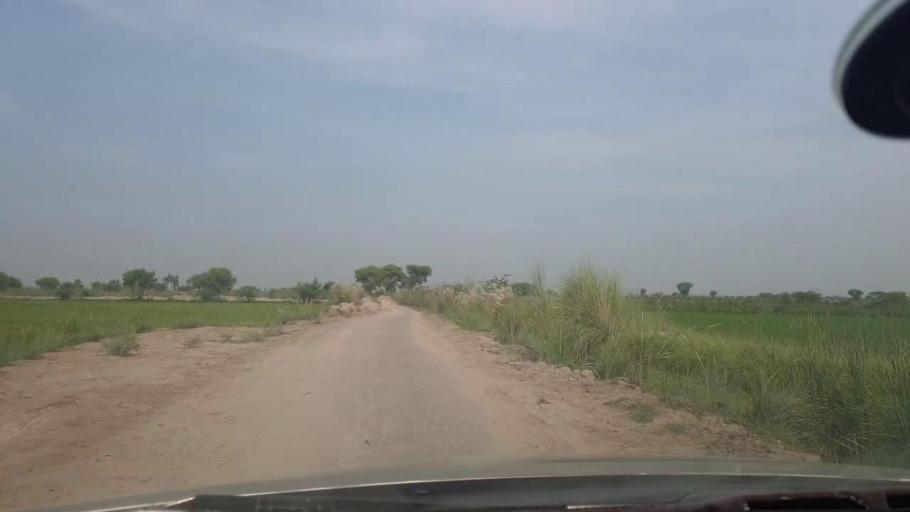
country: PK
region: Sindh
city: Jacobabad
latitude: 28.3112
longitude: 68.4768
